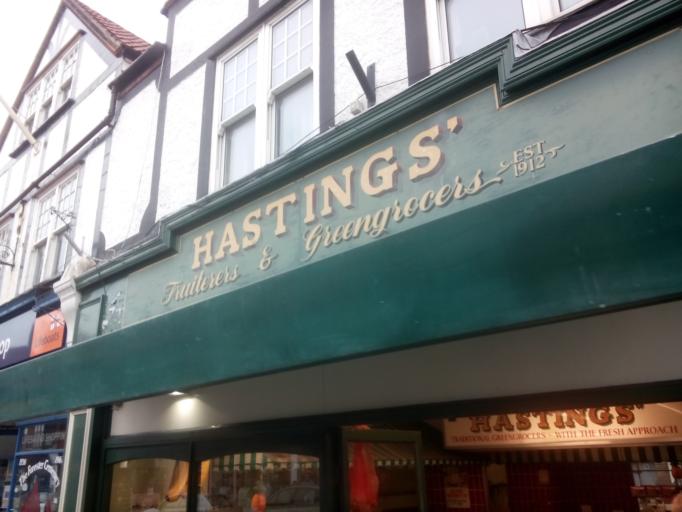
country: GB
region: England
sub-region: Norfolk
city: Sheringham
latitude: 52.9437
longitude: 1.2113
